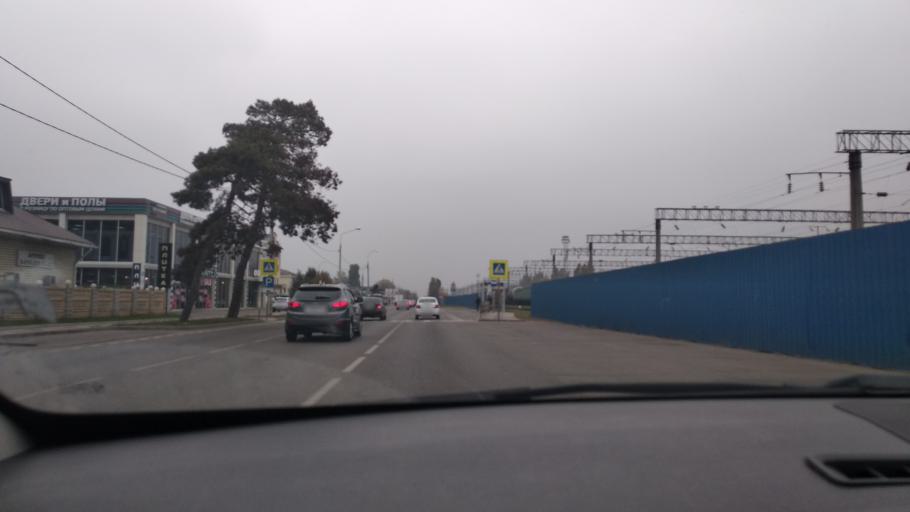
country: RU
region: Krasnodarskiy
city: Pashkovskiy
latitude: 45.0367
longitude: 39.0451
